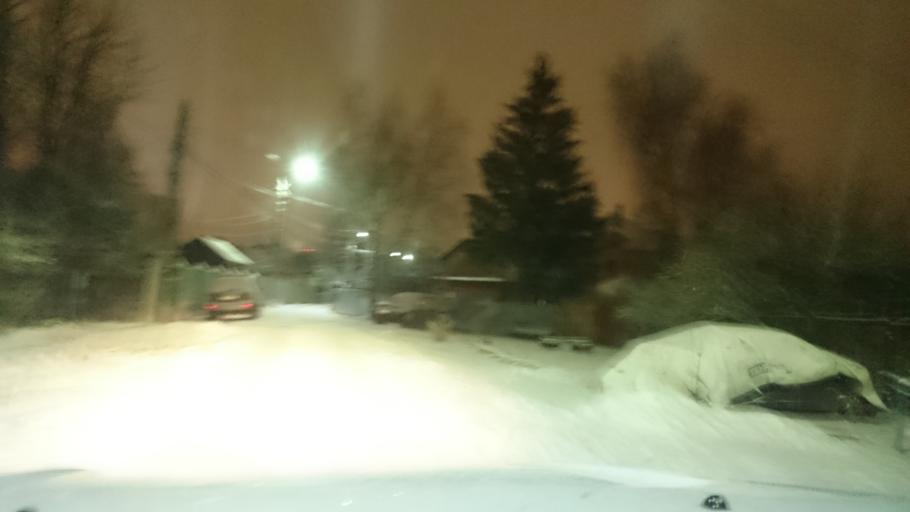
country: RU
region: Tula
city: Tula
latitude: 54.2017
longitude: 37.5643
